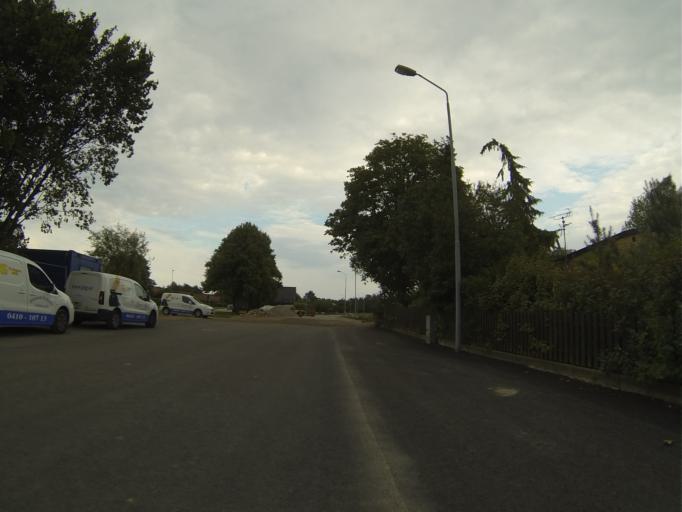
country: SE
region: Skane
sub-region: Staffanstorps Kommun
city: Staffanstorp
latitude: 55.6491
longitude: 13.2142
